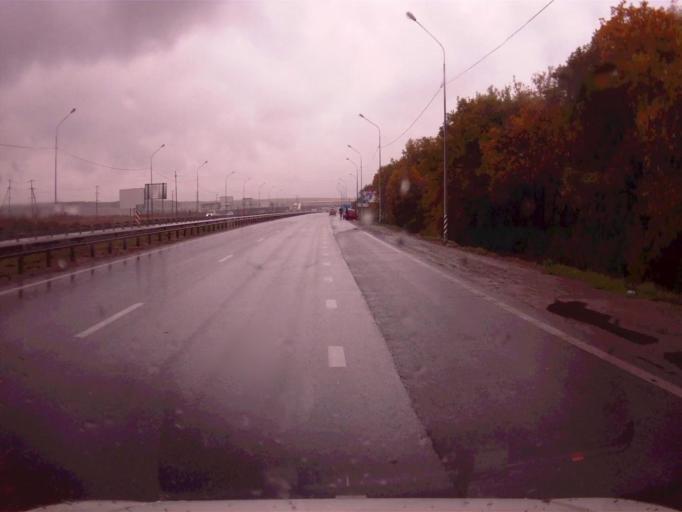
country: RU
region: Chelyabinsk
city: Dolgoderevenskoye
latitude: 55.3067
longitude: 61.3357
